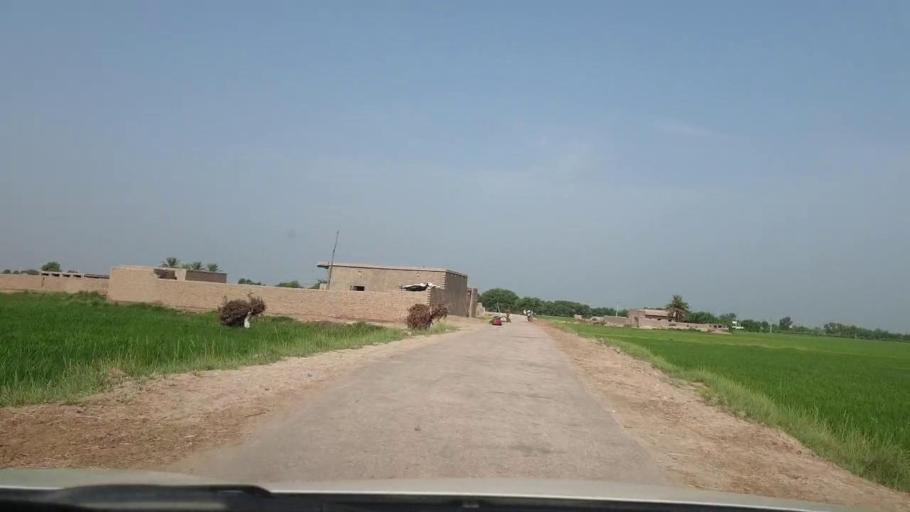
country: PK
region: Sindh
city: Larkana
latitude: 27.4351
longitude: 68.2549
